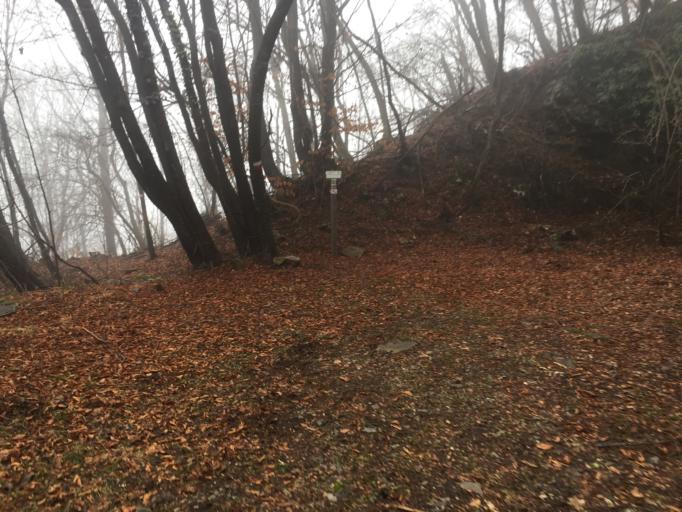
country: IT
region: Friuli Venezia Giulia
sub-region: Provincia di Udine
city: Cras
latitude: 46.1513
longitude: 13.6232
